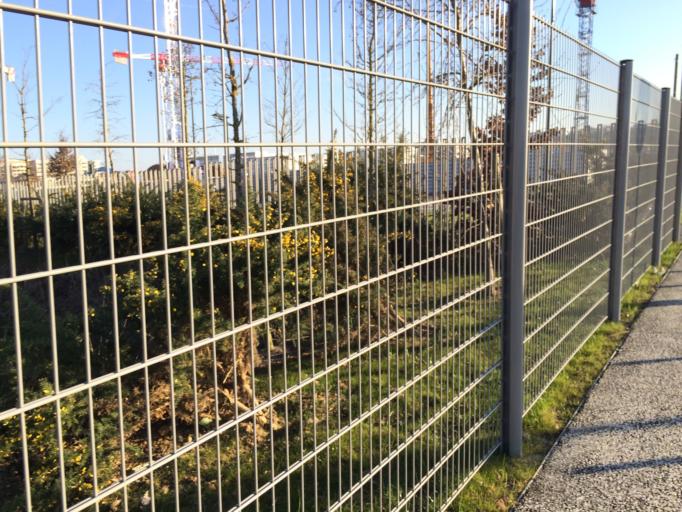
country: FR
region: Ile-de-France
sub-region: Departement de l'Essonne
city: Vauhallan
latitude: 48.7158
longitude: 2.1929
